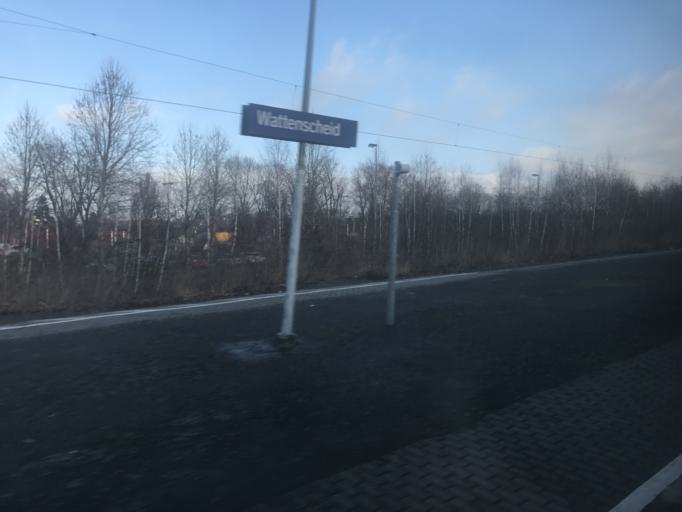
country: DE
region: North Rhine-Westphalia
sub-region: Regierungsbezirk Munster
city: Gelsenkirchen
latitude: 51.4729
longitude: 7.1368
